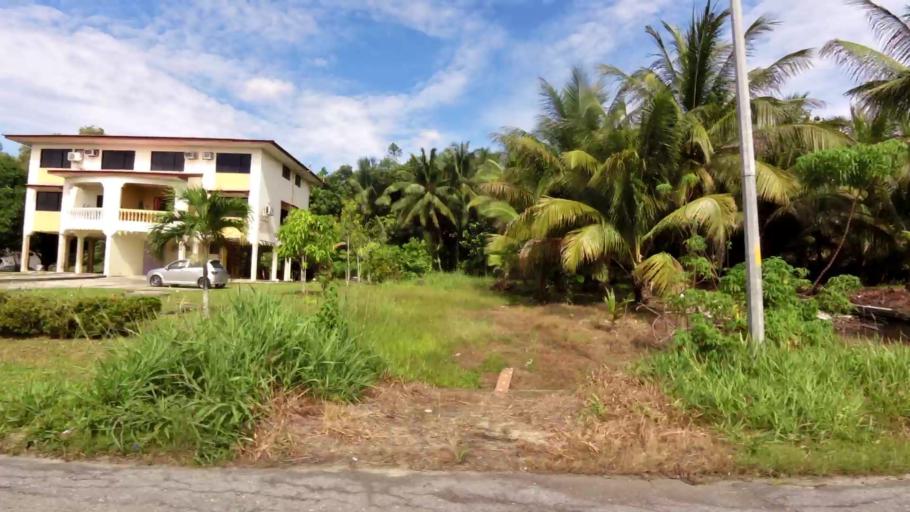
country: BN
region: Brunei and Muara
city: Bandar Seri Begawan
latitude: 4.9341
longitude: 114.9091
